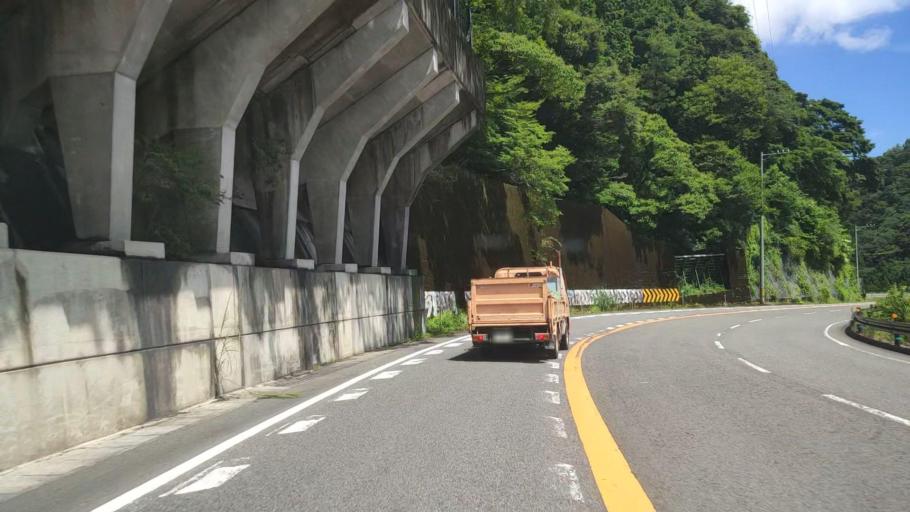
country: JP
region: Mie
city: Owase
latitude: 33.9226
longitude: 136.0960
